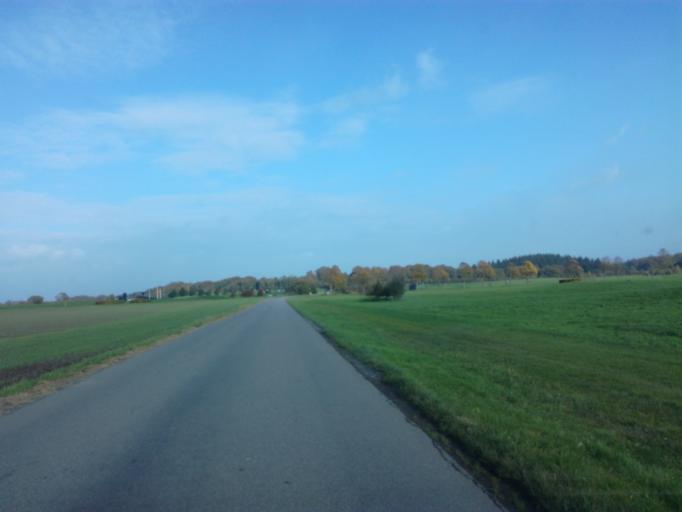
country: DK
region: South Denmark
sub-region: Vejle Kommune
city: Brejning
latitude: 55.6531
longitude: 9.6834
